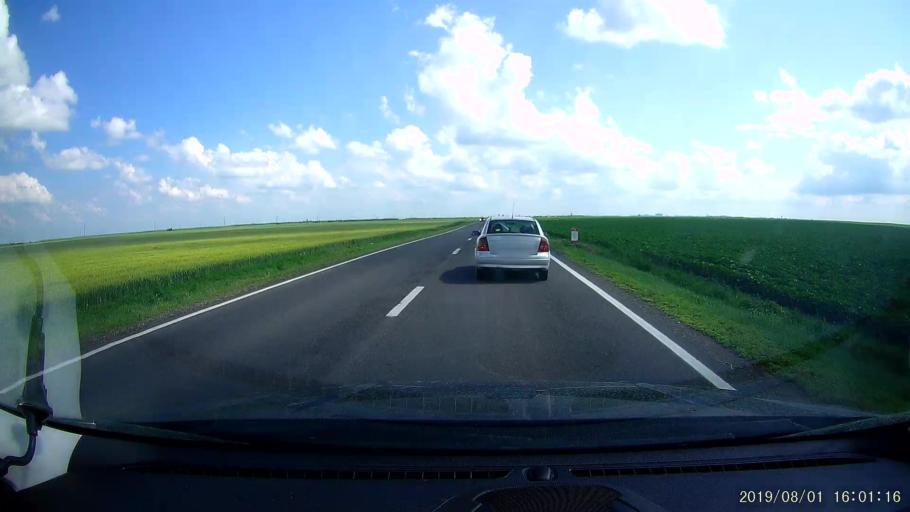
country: RO
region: Ialomita
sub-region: Comuna Ciulnita
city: Ciulnita
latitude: 44.5115
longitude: 27.3901
